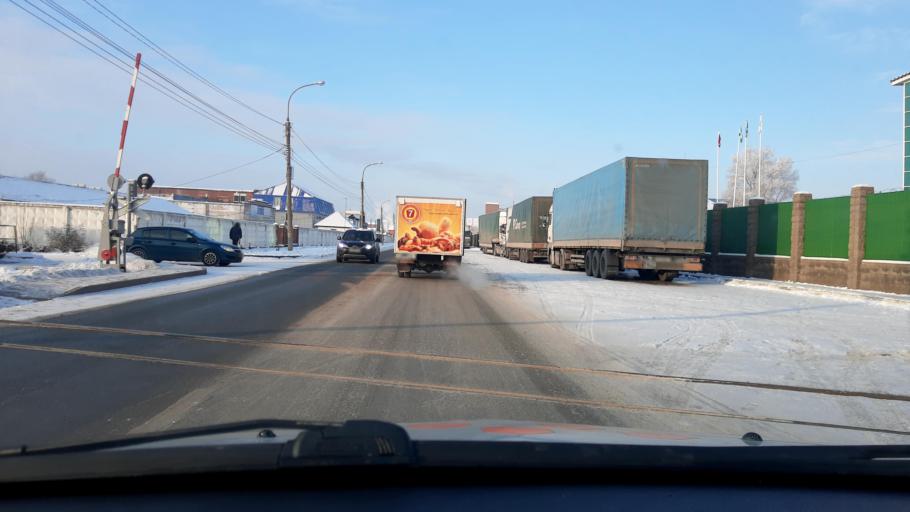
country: RU
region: Bashkortostan
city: Ufa
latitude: 54.8047
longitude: 56.0958
